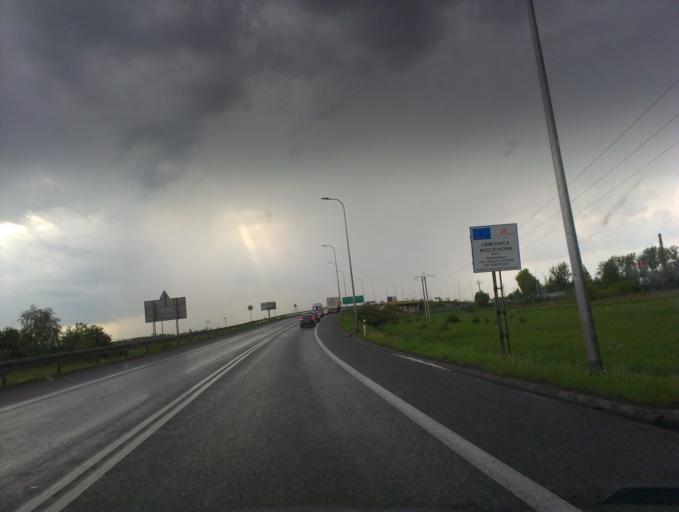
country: PL
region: Masovian Voivodeship
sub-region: Powiat zyrardowski
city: Mszczonow
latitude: 51.9811
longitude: 20.5259
